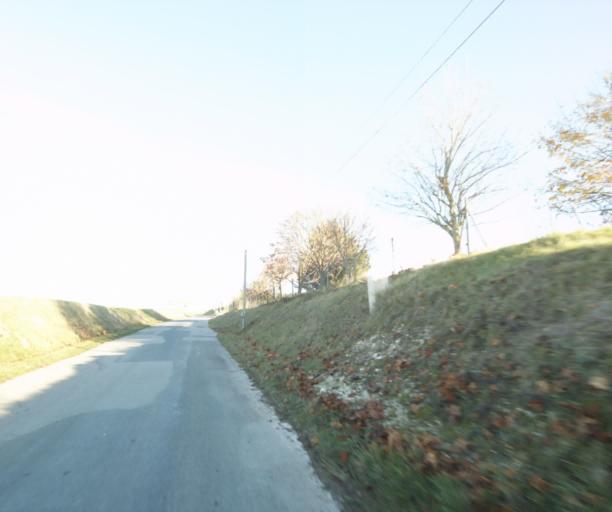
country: FR
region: Poitou-Charentes
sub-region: Departement de la Charente-Maritime
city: Cherac
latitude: 45.7001
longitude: -0.4369
